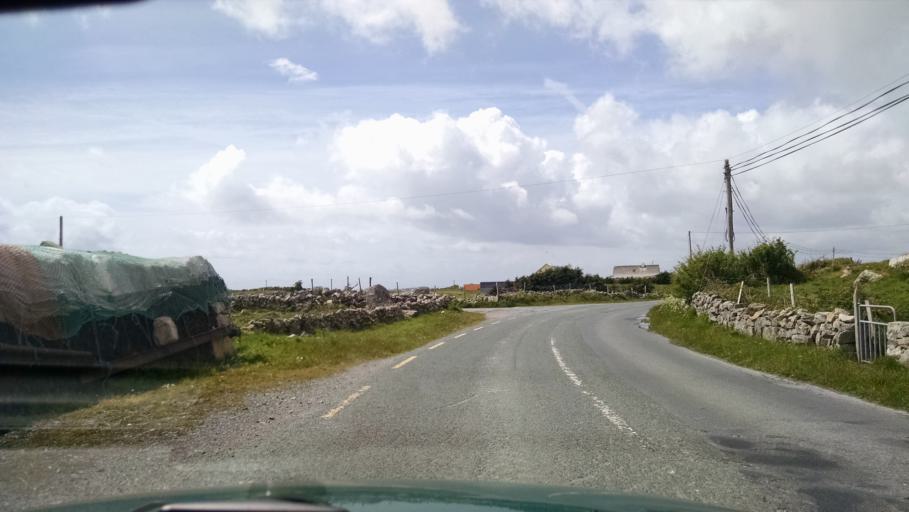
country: IE
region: Connaught
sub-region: County Galway
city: Clifden
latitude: 53.3098
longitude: -9.7926
